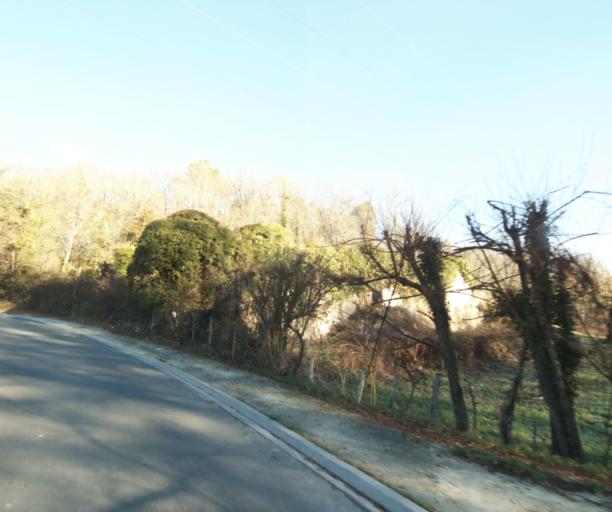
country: FR
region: Poitou-Charentes
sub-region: Departement de la Charente-Maritime
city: Fontcouverte
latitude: 45.7658
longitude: -0.5996
